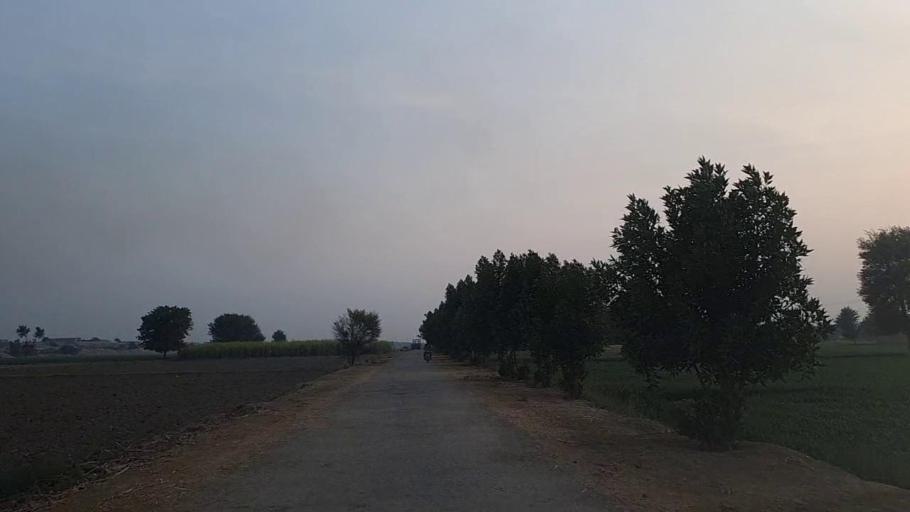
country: PK
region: Sindh
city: Jam Sahib
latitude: 26.4632
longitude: 68.5348
